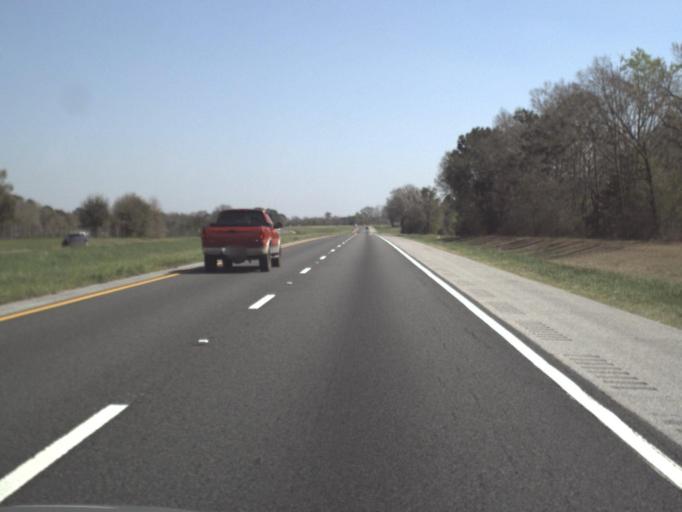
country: US
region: Florida
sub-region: Jackson County
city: Sneads
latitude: 30.6467
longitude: -85.0104
